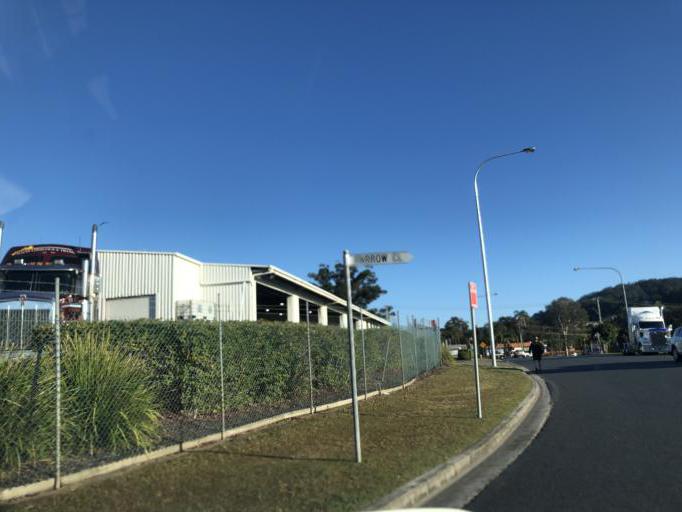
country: AU
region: New South Wales
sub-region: Coffs Harbour
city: Coffs Harbour
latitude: -30.3095
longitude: 153.1014
